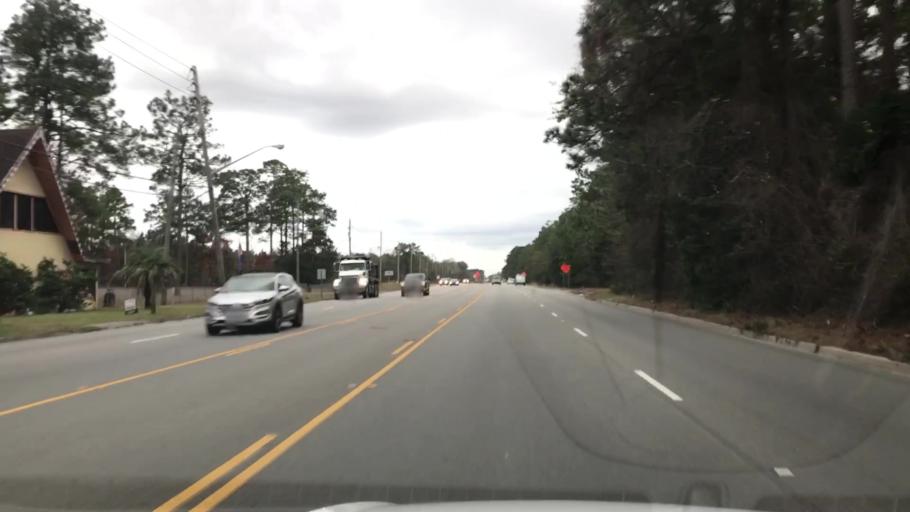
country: US
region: South Carolina
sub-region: Georgetown County
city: Georgetown
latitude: 33.3386
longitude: -79.3045
